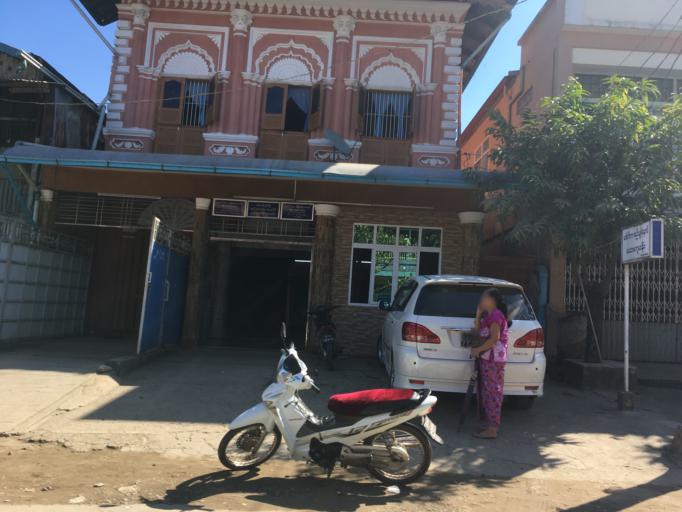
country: MM
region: Mon
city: Mawlamyine
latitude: 16.4926
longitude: 97.6329
